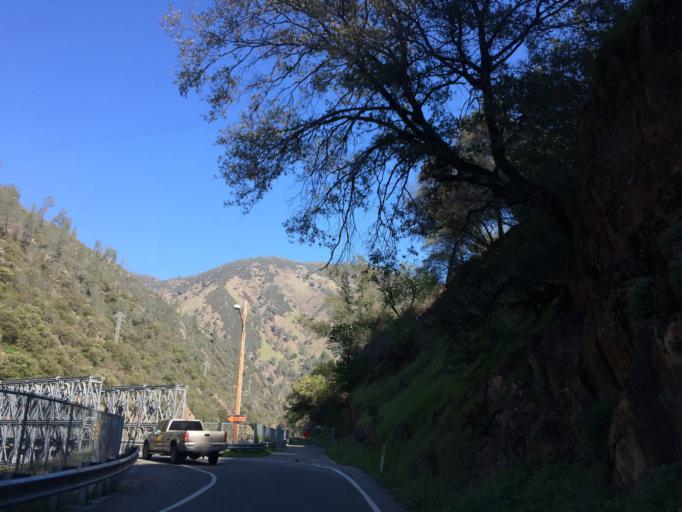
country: US
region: California
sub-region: Mariposa County
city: Midpines
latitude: 37.6594
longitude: -119.9002
